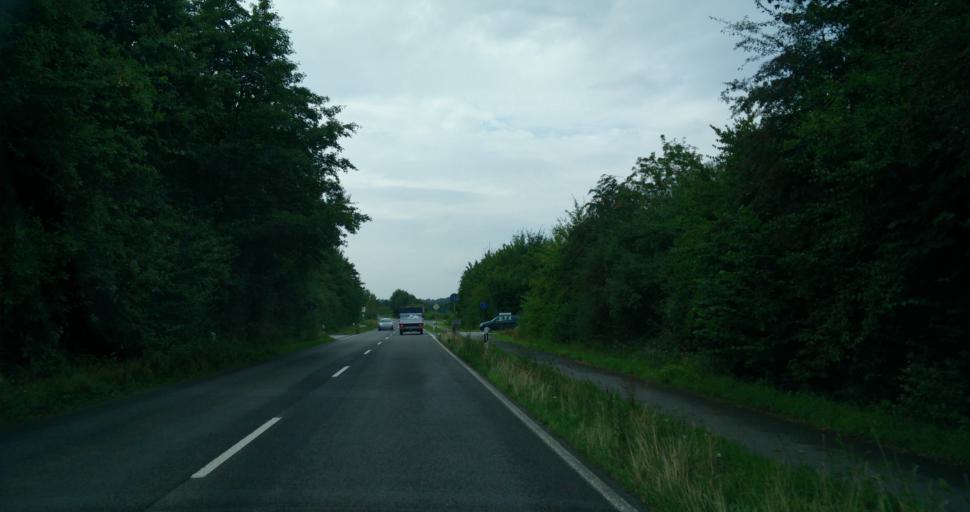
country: DE
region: North Rhine-Westphalia
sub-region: Regierungsbezirk Dusseldorf
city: Erkrath
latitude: 51.2720
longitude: 6.9150
